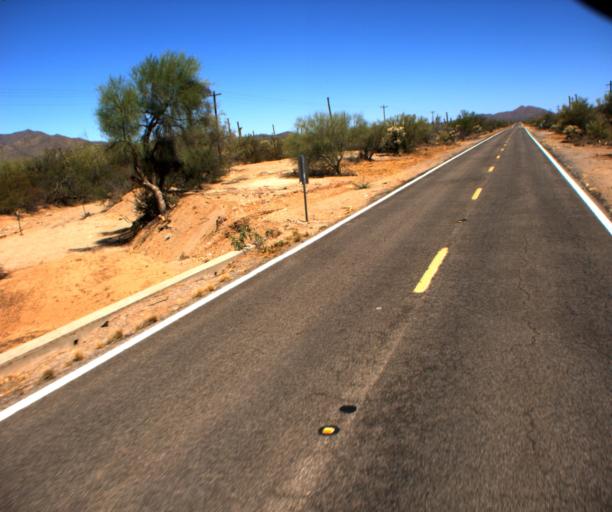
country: US
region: Arizona
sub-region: Pima County
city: Sells
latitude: 32.1243
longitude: -112.0850
